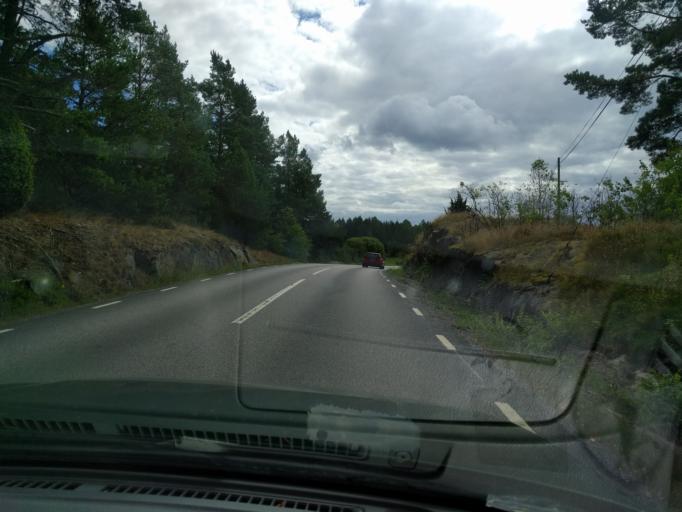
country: SE
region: Soedermanland
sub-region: Nykopings Kommun
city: Svalsta
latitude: 58.5169
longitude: 16.8475
